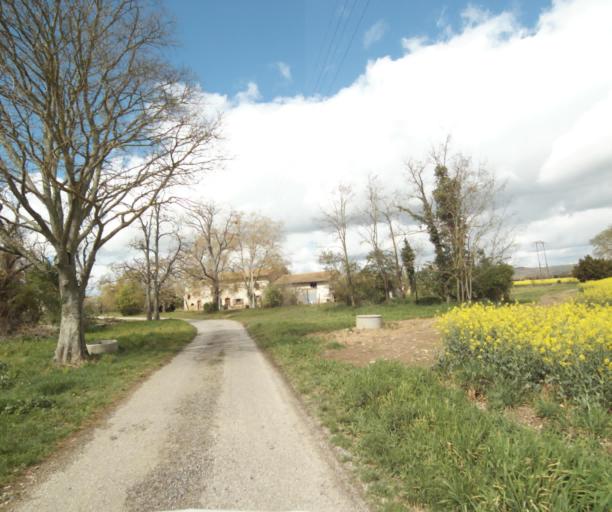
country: FR
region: Midi-Pyrenees
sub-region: Departement de l'Ariege
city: Saverdun
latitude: 43.2639
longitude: 1.5948
